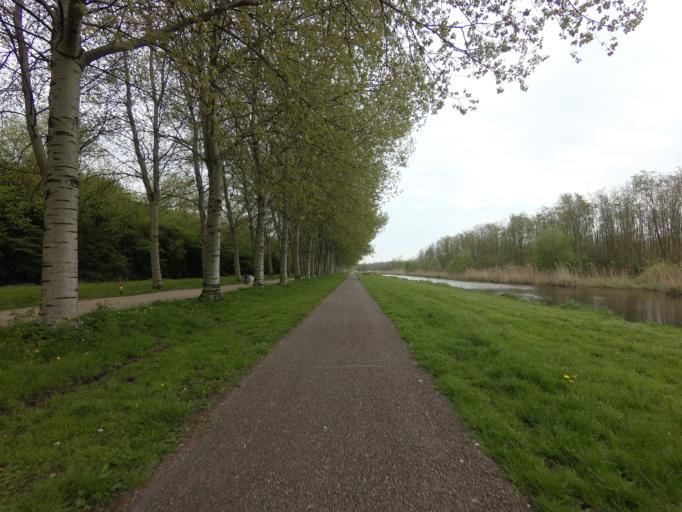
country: NL
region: North Holland
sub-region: Gemeente Diemen
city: Diemen
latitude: 52.3323
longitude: 4.9901
